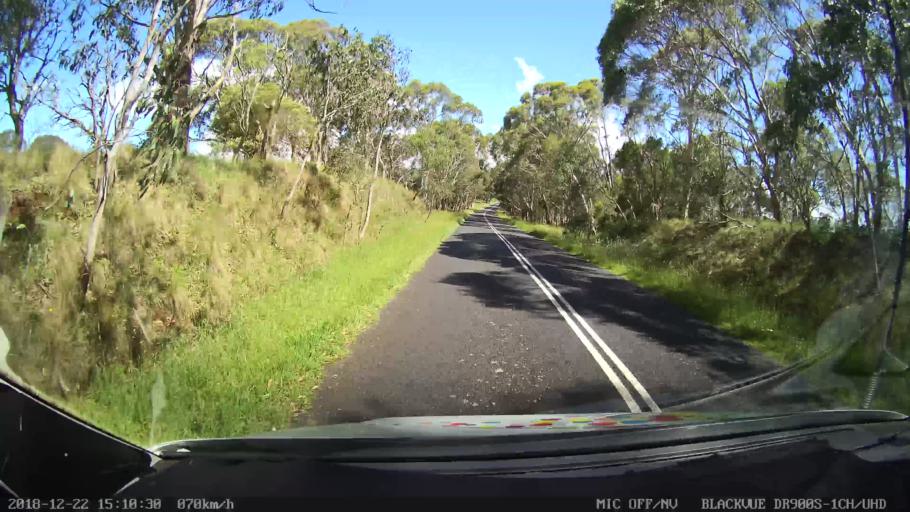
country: AU
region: New South Wales
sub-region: Bellingen
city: Dorrigo
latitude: -30.3355
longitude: 152.4059
